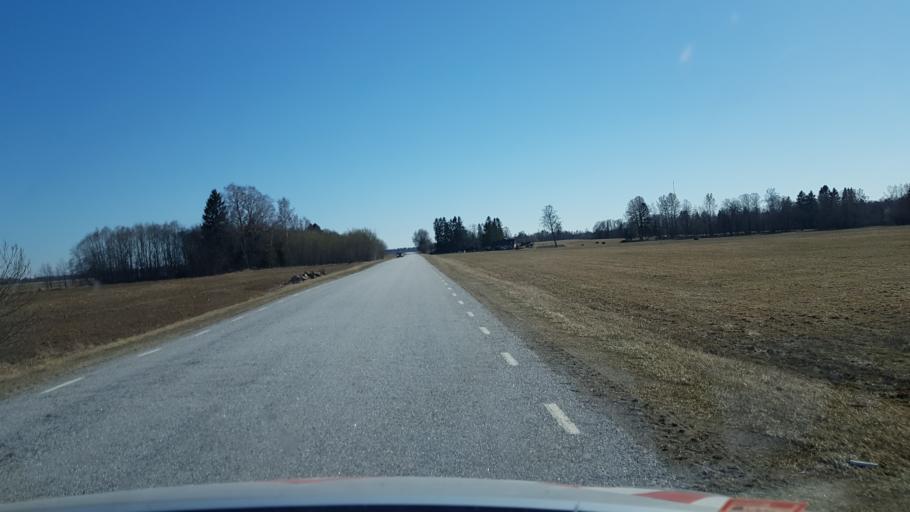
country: EE
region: Jaervamaa
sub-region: Koeru vald
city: Koeru
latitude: 59.0193
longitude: 26.0882
